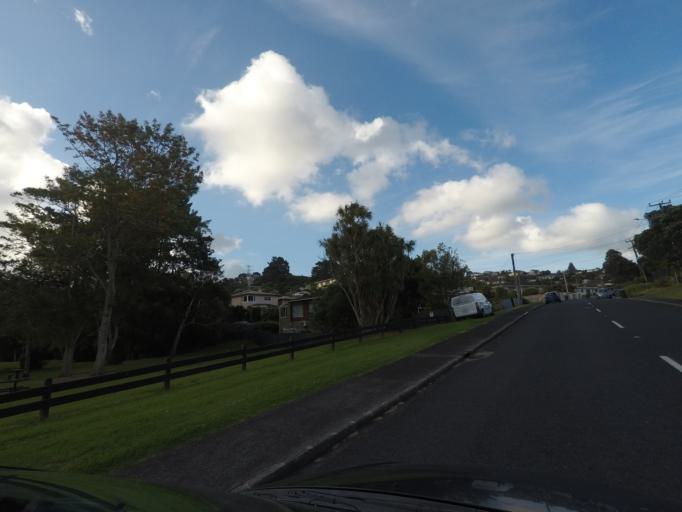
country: NZ
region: Auckland
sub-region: Auckland
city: Mangere
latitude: -36.9274
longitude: 174.7597
